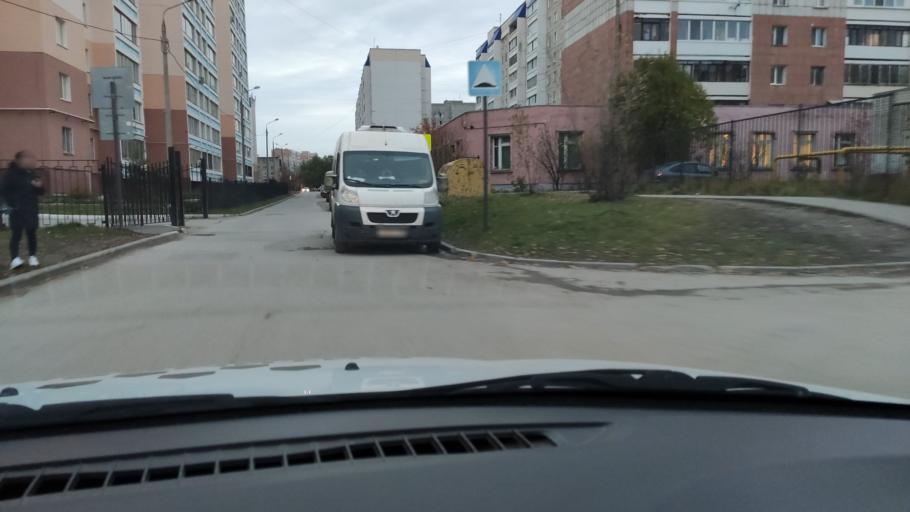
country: RU
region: Perm
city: Kondratovo
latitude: 58.0387
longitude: 56.1200
